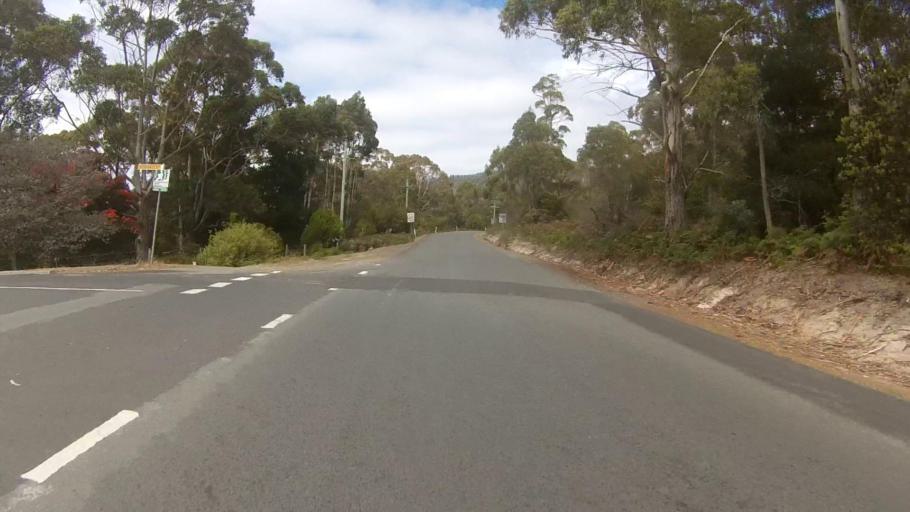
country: AU
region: Tasmania
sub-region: Kingborough
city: Blackmans Bay
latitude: -43.0137
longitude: 147.3234
